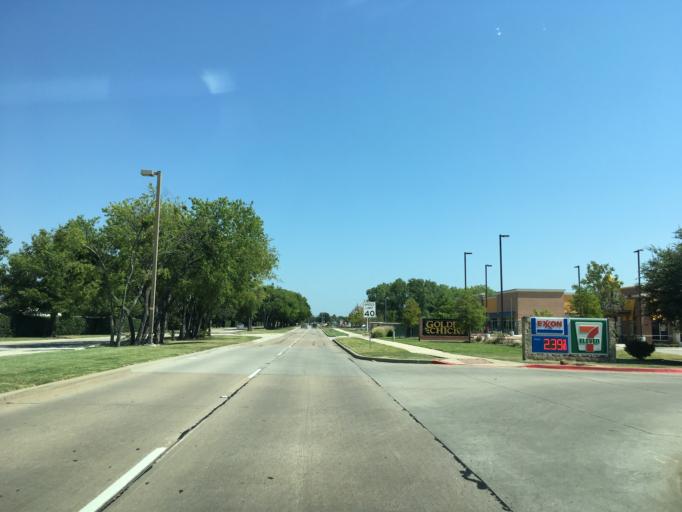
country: US
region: Texas
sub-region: Collin County
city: Fairview
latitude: 33.1597
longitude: -96.6805
